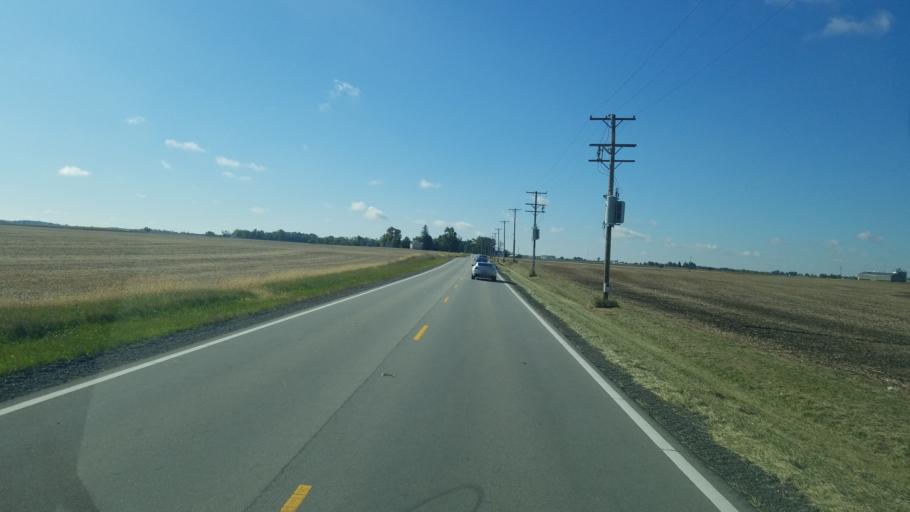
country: US
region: Ohio
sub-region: Fayette County
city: Washington Court House
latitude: 39.4681
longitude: -83.4866
